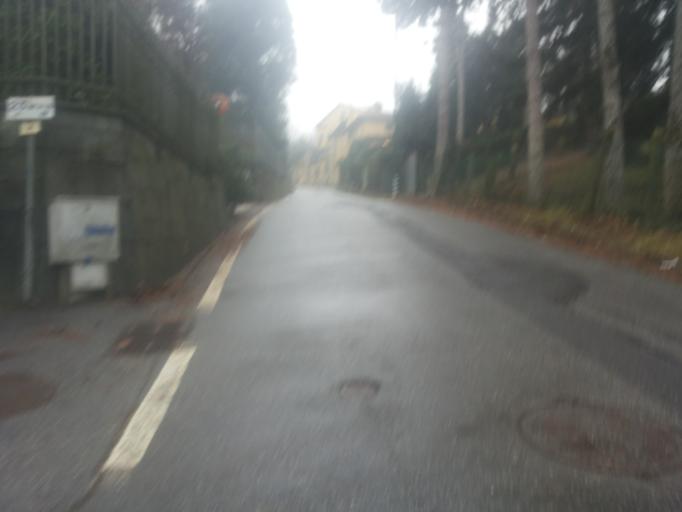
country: IT
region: Piedmont
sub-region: Provincia di Torino
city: Turin
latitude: 45.0497
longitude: 7.7095
